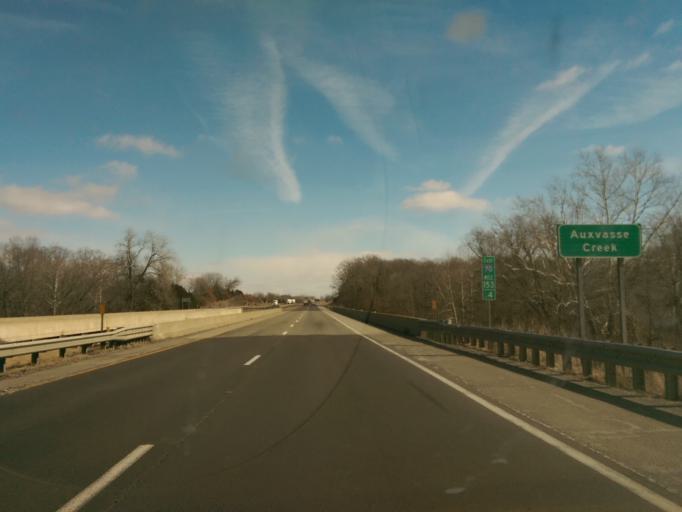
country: US
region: Missouri
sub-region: Callaway County
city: Fulton
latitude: 38.9359
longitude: -91.8447
